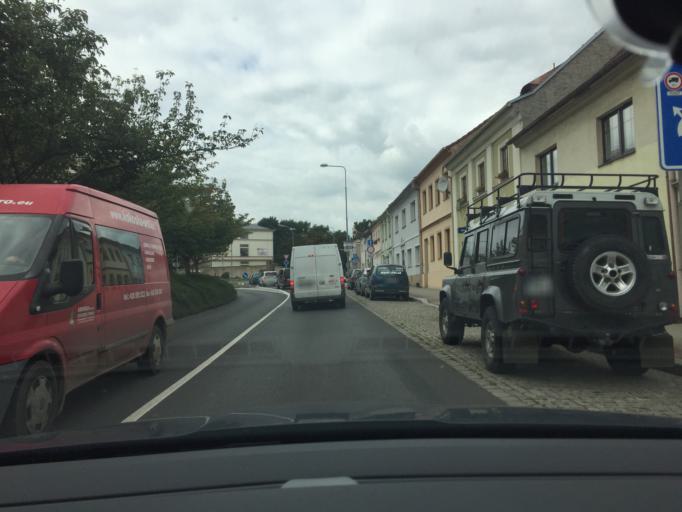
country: CZ
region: Ustecky
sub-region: Okres Litomerice
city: Litomerice
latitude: 50.5370
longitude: 14.1298
